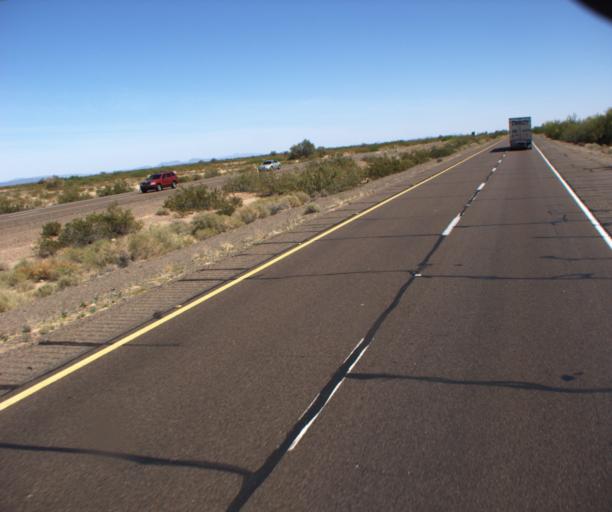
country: US
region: Arizona
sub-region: Yuma County
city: Wellton
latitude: 32.8195
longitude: -113.4807
